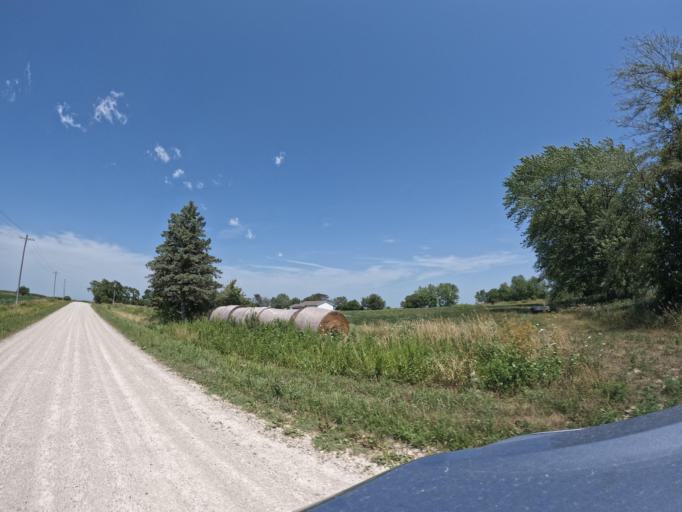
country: US
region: Iowa
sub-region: Henry County
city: Mount Pleasant
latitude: 40.9433
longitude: -91.6461
